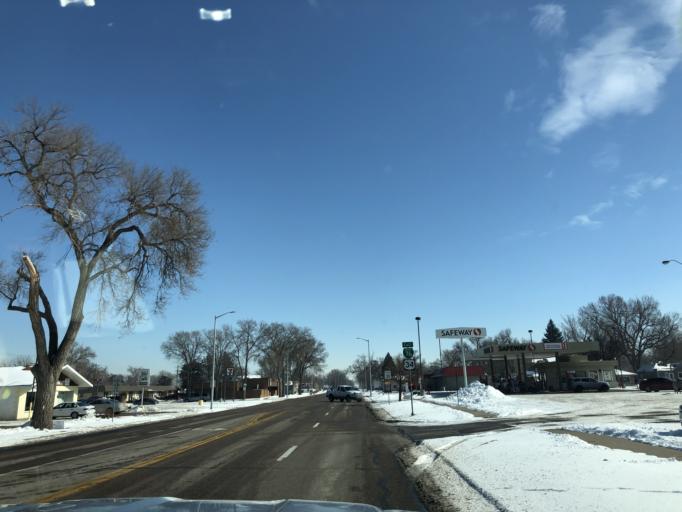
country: US
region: Colorado
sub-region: Morgan County
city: Fort Morgan
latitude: 40.2540
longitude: -103.8110
